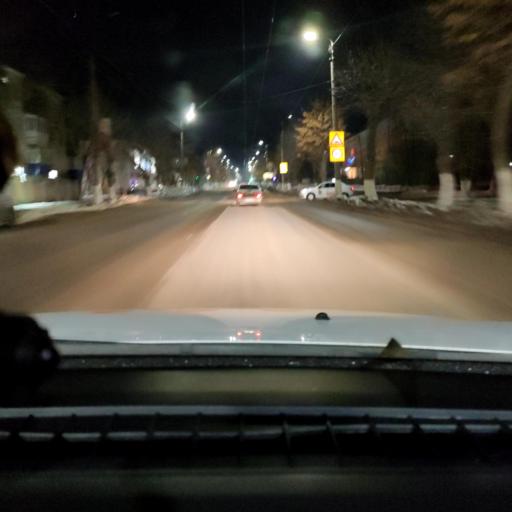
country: RU
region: Samara
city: Novokuybyshevsk
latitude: 53.0896
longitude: 49.9502
